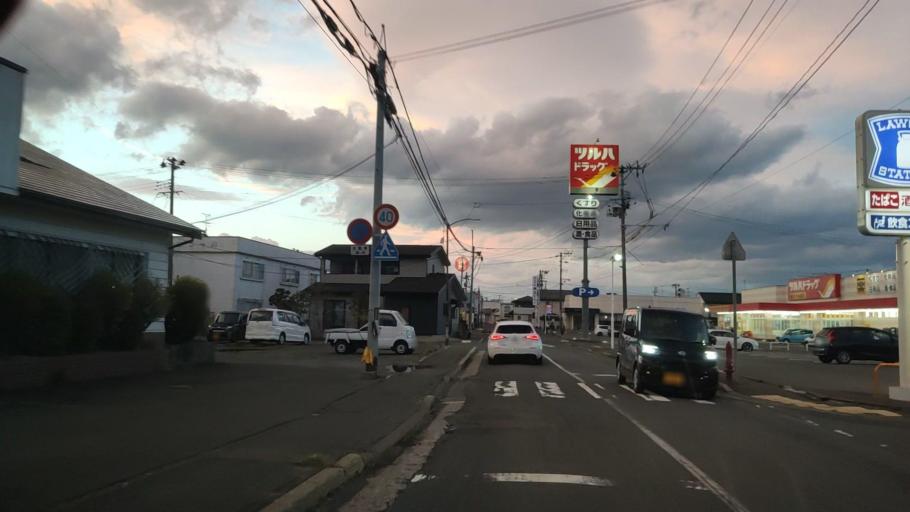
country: JP
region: Iwate
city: Morioka-shi
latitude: 39.7131
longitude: 141.1101
